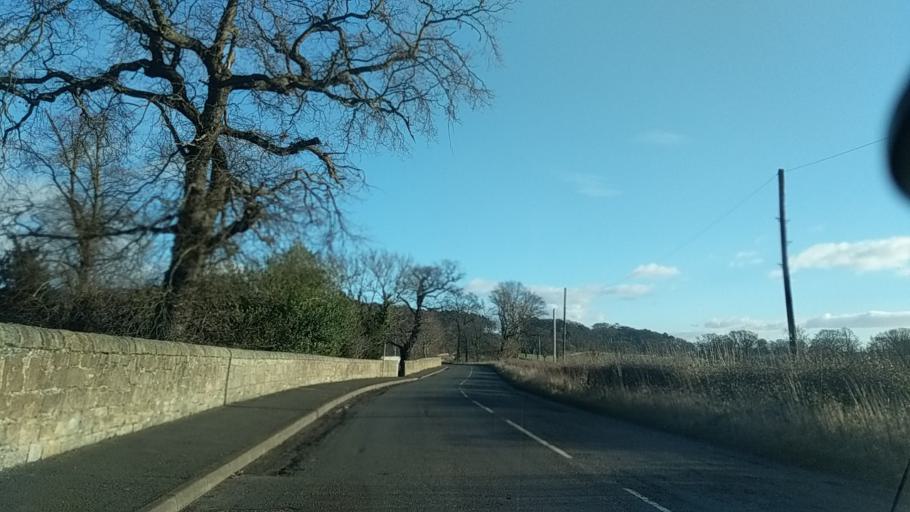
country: GB
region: Scotland
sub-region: Edinburgh
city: Queensferry
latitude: 55.9891
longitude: -3.3758
